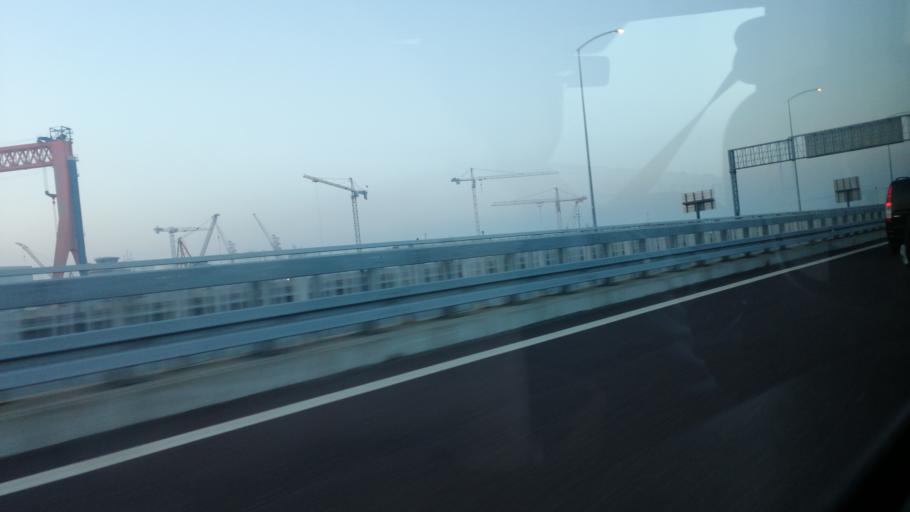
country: TR
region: Yalova
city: Altinova
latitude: 40.7287
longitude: 29.5060
